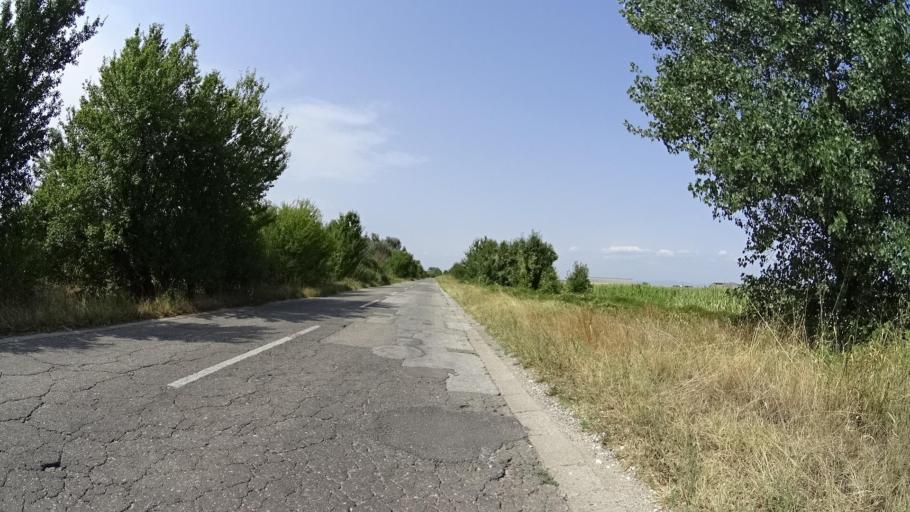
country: BG
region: Plovdiv
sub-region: Obshtina Plovdiv
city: Plovdiv
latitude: 42.2274
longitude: 24.7862
